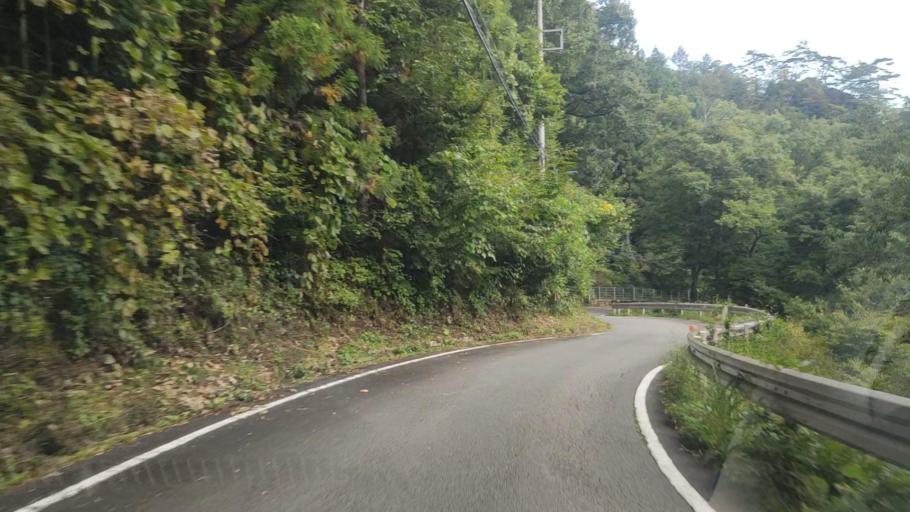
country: JP
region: Gunma
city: Nakanojomachi
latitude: 36.6503
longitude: 138.6401
